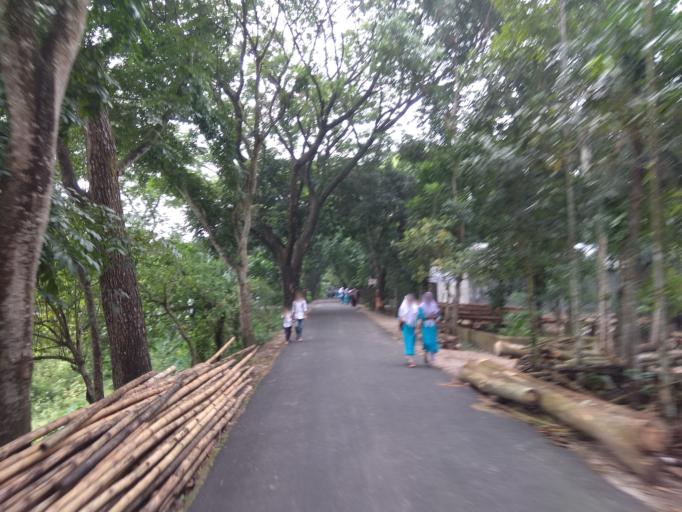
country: BD
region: Dhaka
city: Dohar
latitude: 23.4708
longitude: 90.0748
